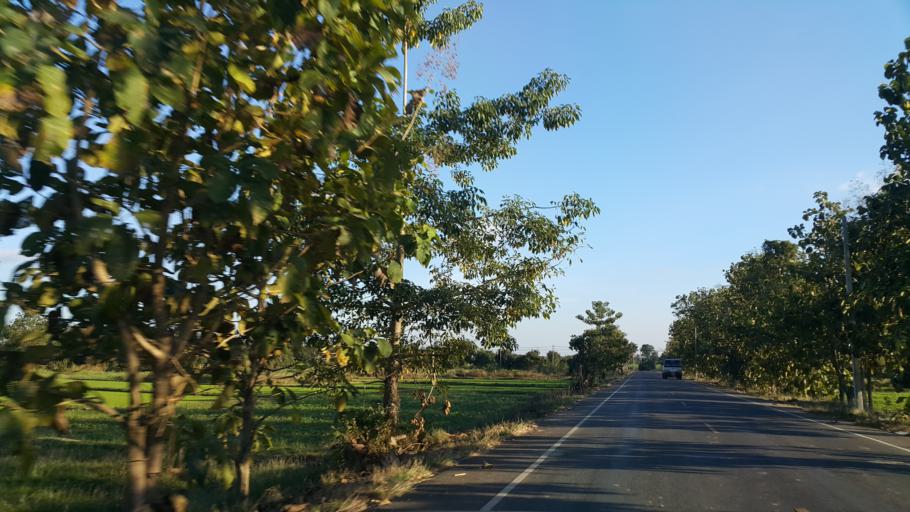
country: TH
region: Sukhothai
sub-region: Amphoe Si Satchanalai
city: Si Satchanalai
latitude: 17.5388
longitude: 99.7987
